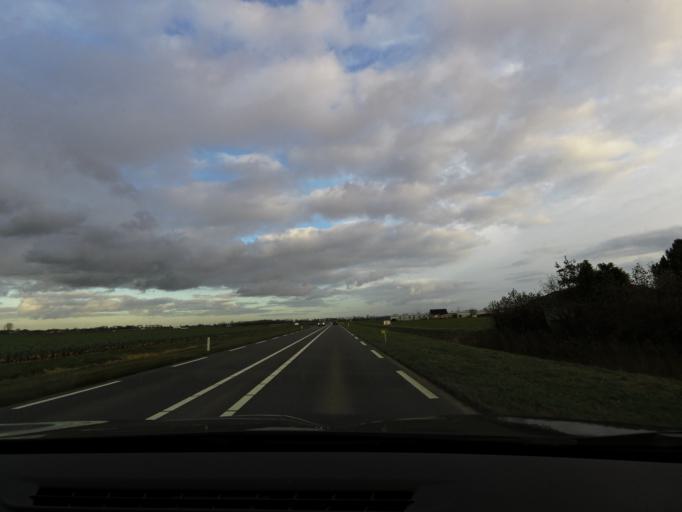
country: NL
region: South Holland
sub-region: Gemeente Oud-Beijerland
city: Oud-Beijerland
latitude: 51.8107
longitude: 4.4424
